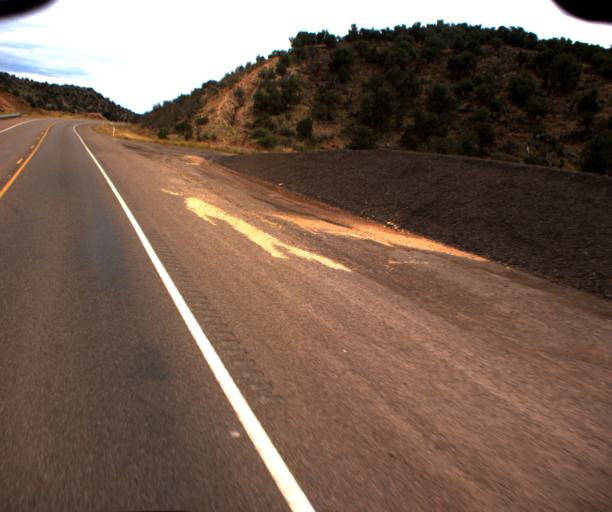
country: US
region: Arizona
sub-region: Navajo County
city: Taylor
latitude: 34.4007
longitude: -110.0715
